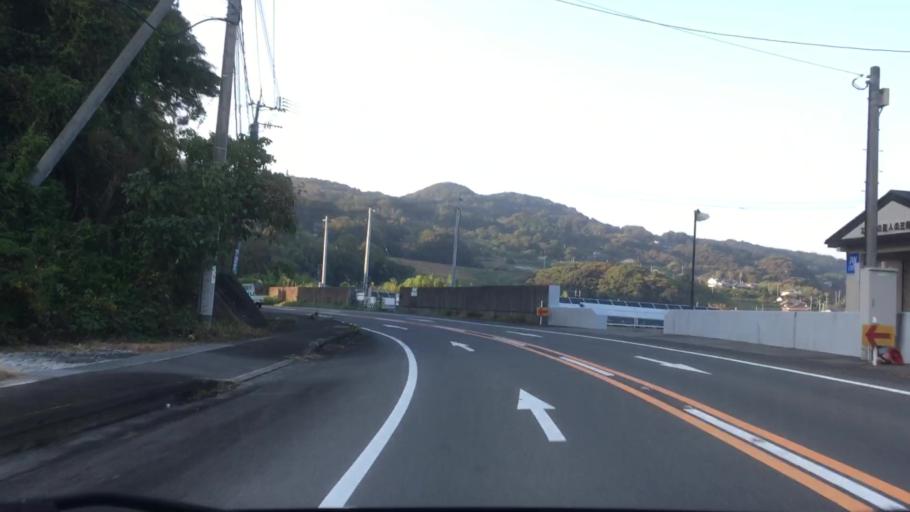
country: JP
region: Nagasaki
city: Sasebo
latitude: 33.0136
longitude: 129.7345
